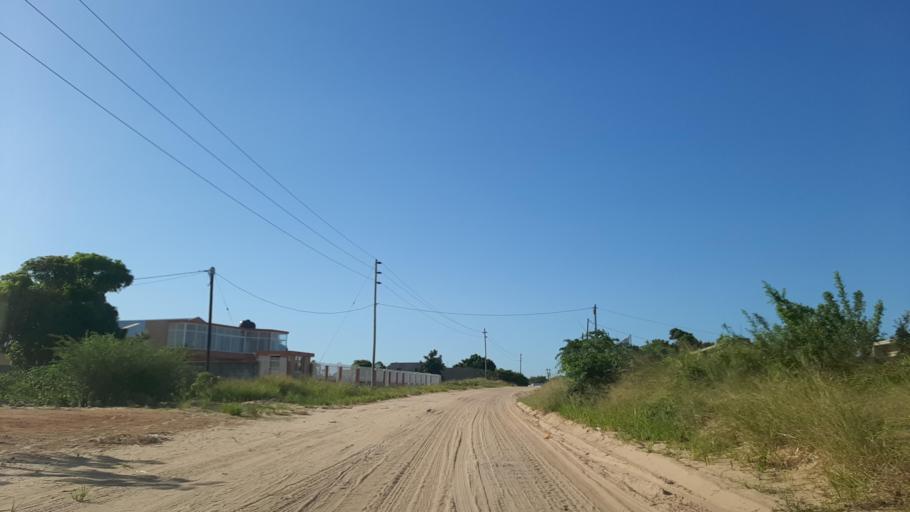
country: MZ
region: Maputo City
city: Maputo
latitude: -25.7556
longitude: 32.5502
